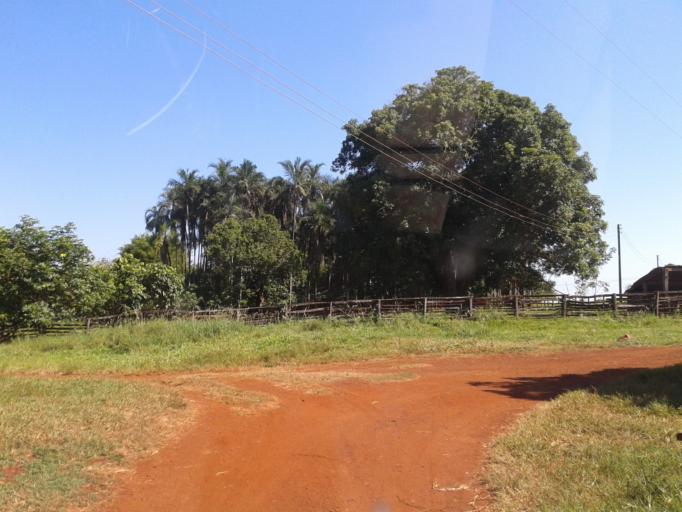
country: BR
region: Minas Gerais
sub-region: Centralina
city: Centralina
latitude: -18.6518
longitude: -49.2978
